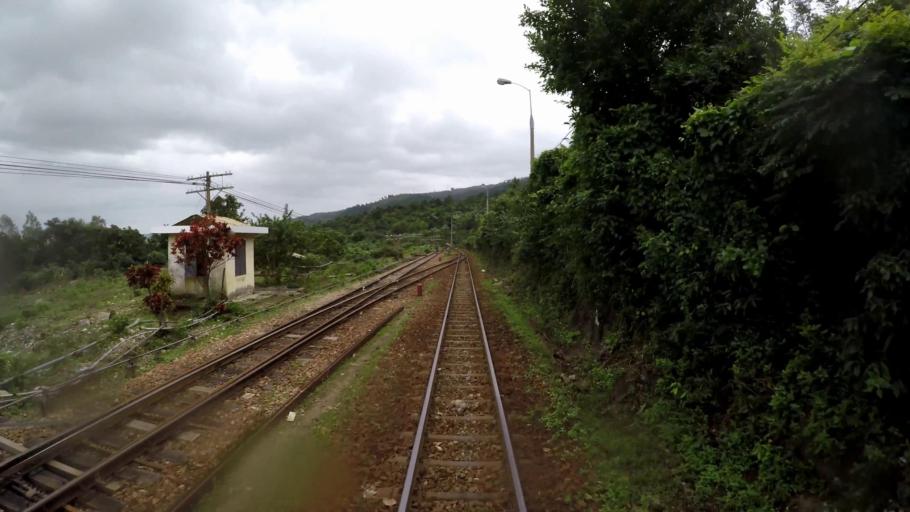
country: VN
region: Da Nang
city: Lien Chieu
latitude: 16.1661
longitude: 108.1356
